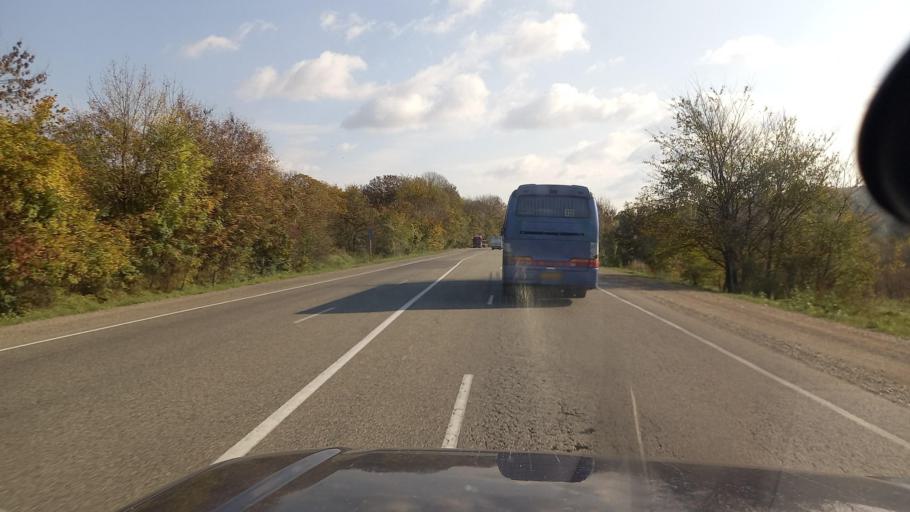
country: RU
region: Krasnodarskiy
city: Gayduk
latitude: 44.8739
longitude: 37.7635
